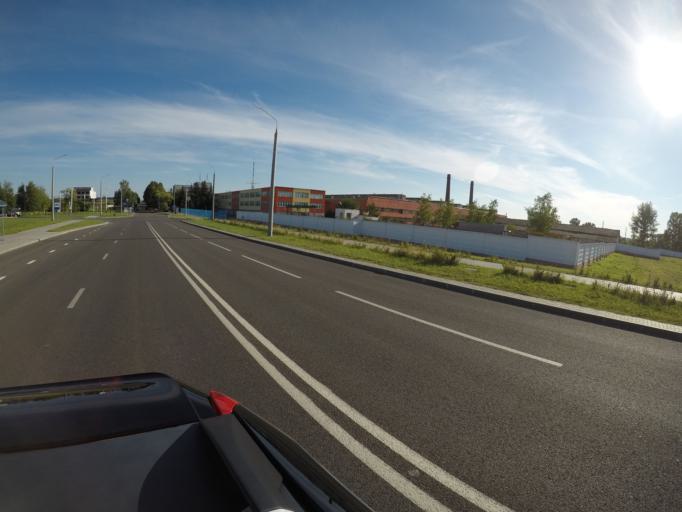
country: BY
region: Grodnenskaya
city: Hrodna
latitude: 53.7156
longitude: 23.8250
